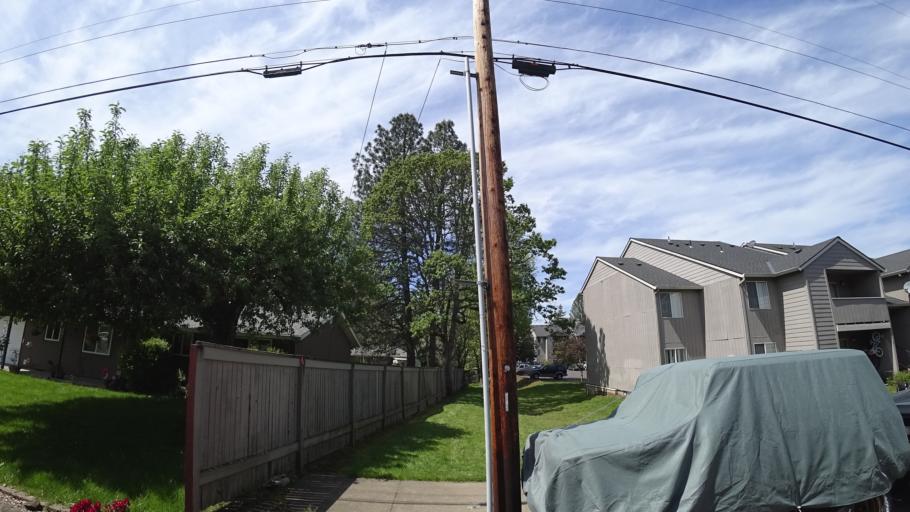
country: US
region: Oregon
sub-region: Washington County
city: Aloha
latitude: 45.4917
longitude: -122.8567
